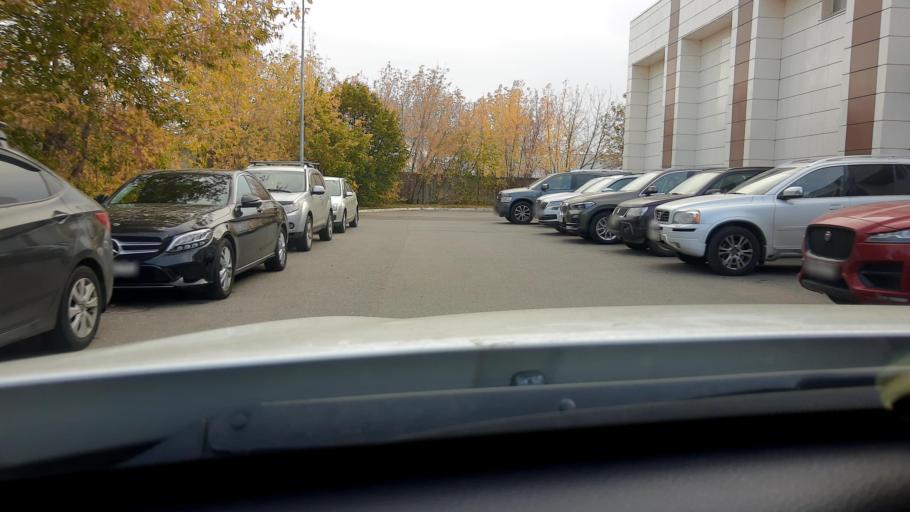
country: RU
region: Moskovskaya
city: Bogorodskoye
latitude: 55.8073
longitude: 37.7397
